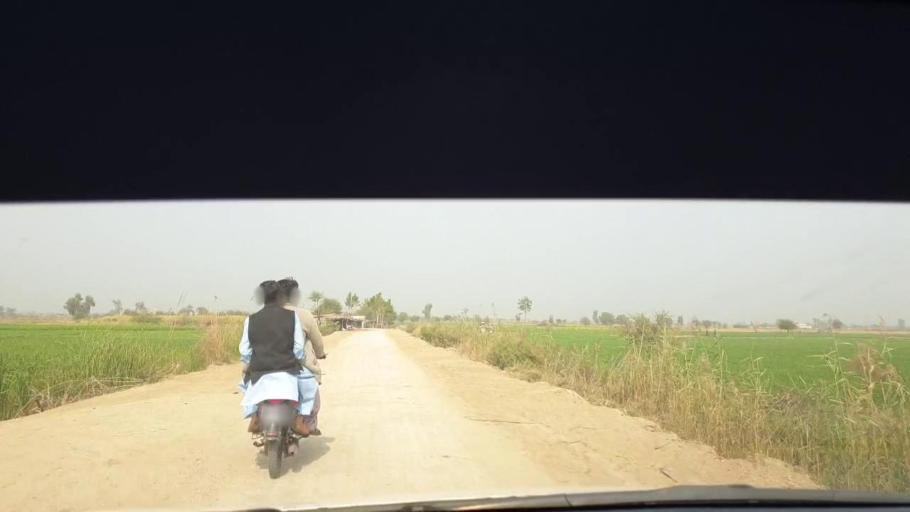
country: PK
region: Sindh
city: Berani
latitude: 25.8181
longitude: 68.8434
